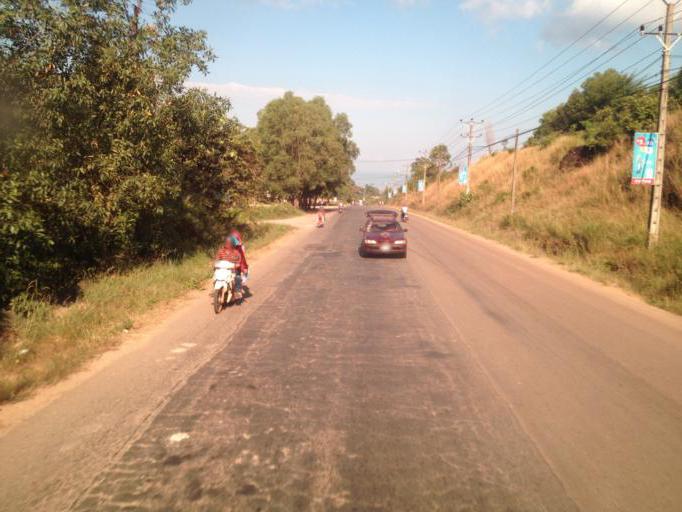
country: KH
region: Preah Sihanouk
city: Sihanoukville
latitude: 10.6387
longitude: 103.5308
